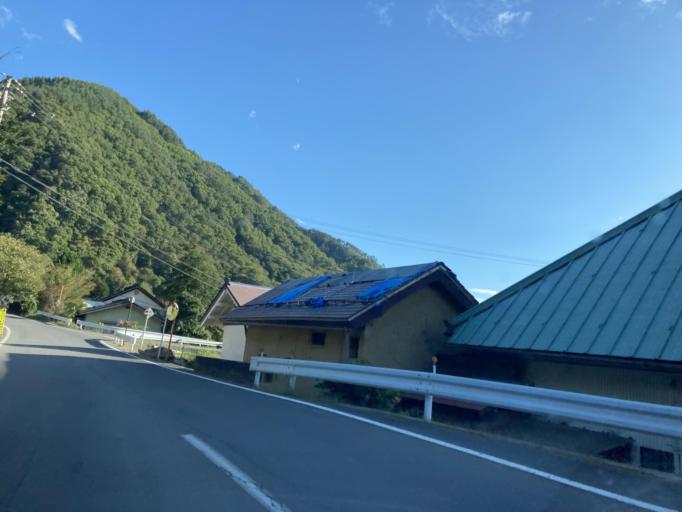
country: JP
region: Nagano
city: Omachi
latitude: 36.4672
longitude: 137.9475
